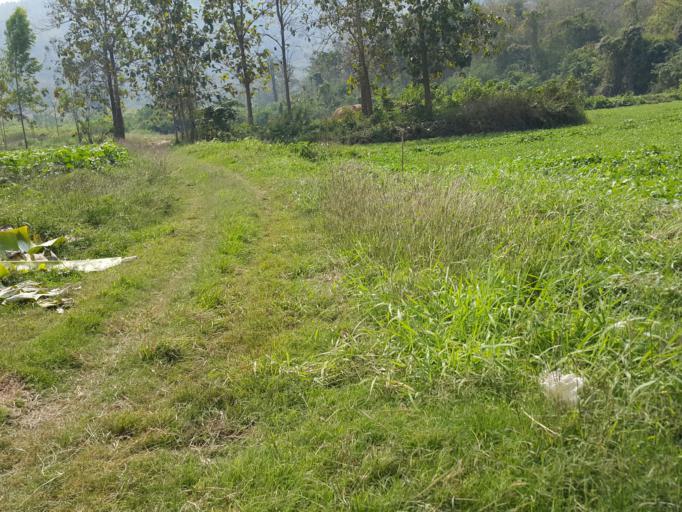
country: TH
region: Sukhothai
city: Thung Saliam
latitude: 17.3287
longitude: 99.4929
